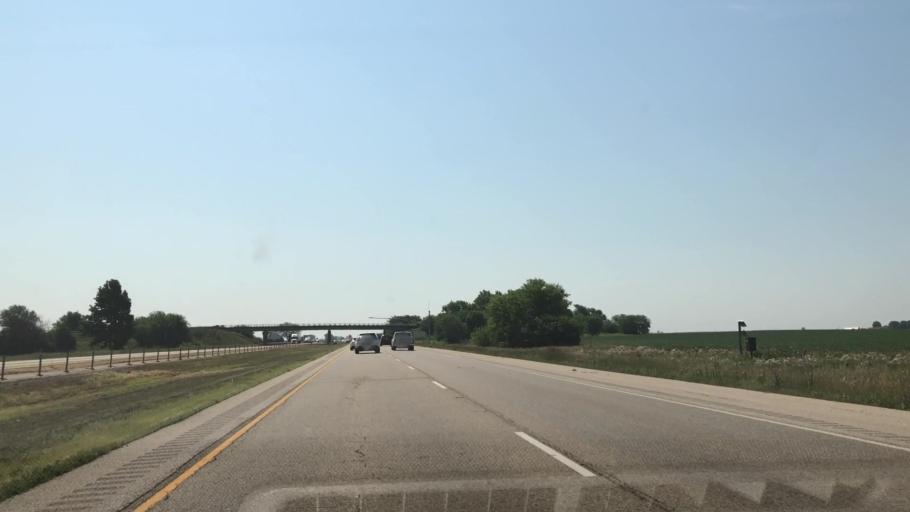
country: US
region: Illinois
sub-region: McLean County
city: Danvers
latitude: 40.5675
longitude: -89.1212
